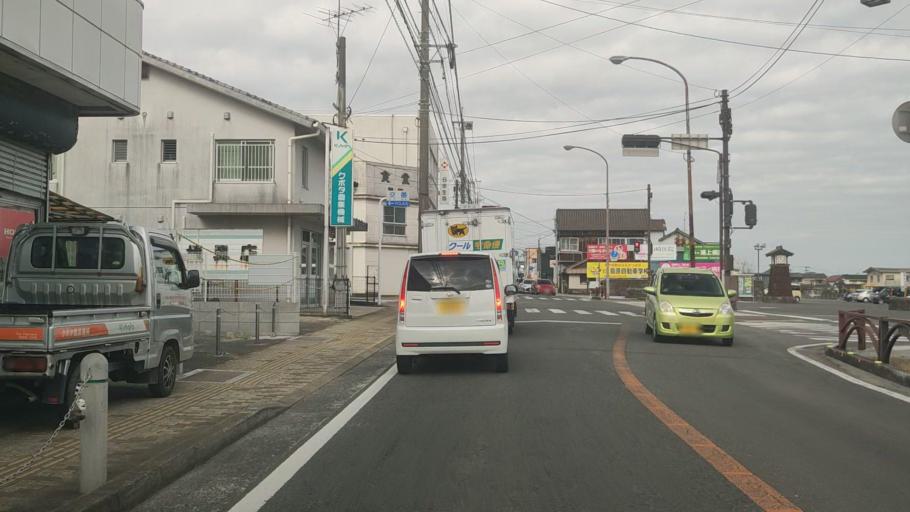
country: JP
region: Nagasaki
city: Shimabara
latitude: 32.7897
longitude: 130.3703
